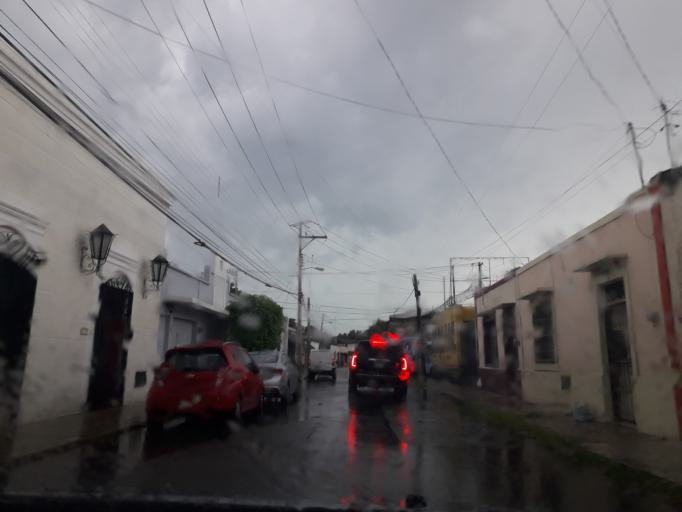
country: MX
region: Yucatan
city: Merida
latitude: 20.9691
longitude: -89.6335
